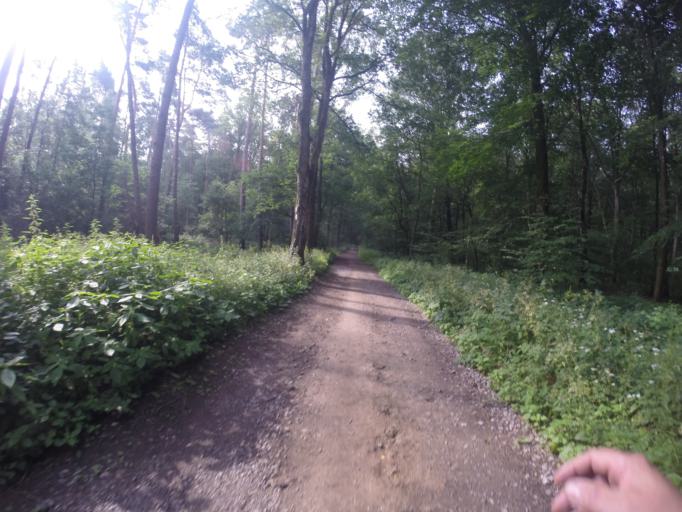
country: DE
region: North Rhine-Westphalia
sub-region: Regierungsbezirk Dusseldorf
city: Emmerich
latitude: 51.8743
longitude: 6.1826
